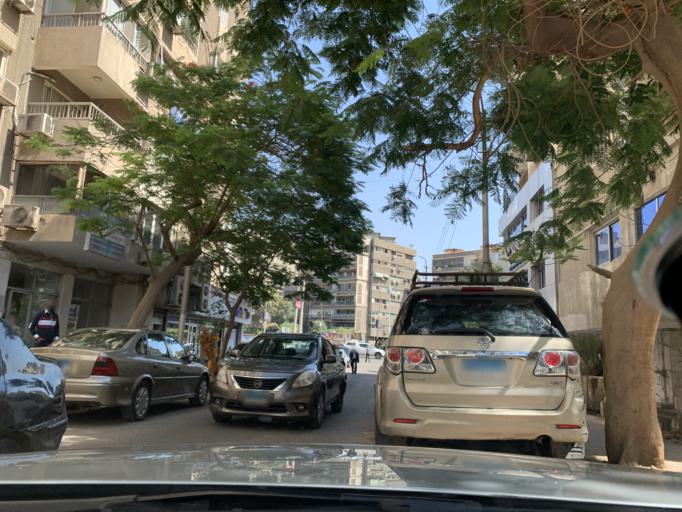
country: EG
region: Muhafazat al Qahirah
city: Cairo
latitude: 30.0856
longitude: 31.3310
